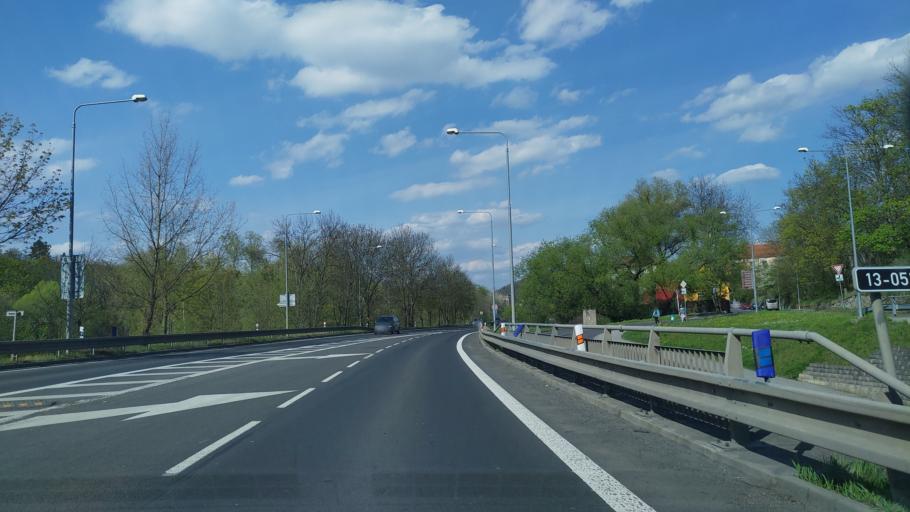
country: CZ
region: Ustecky
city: Bilina Kyselka
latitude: 50.5416
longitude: 13.7633
